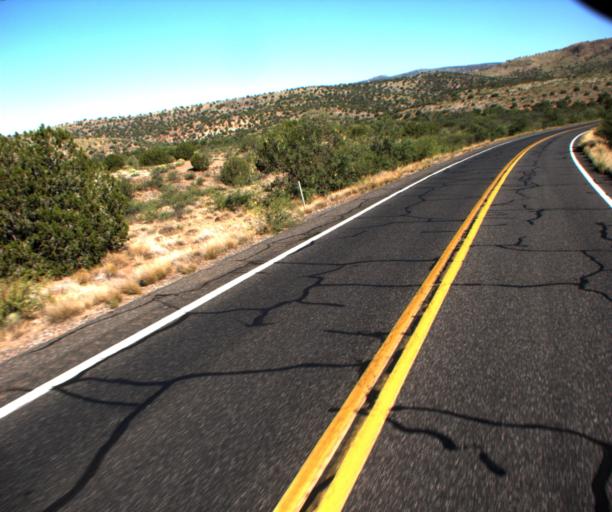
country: US
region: Arizona
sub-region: Yavapai County
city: Big Park
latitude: 34.7121
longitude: -111.7771
